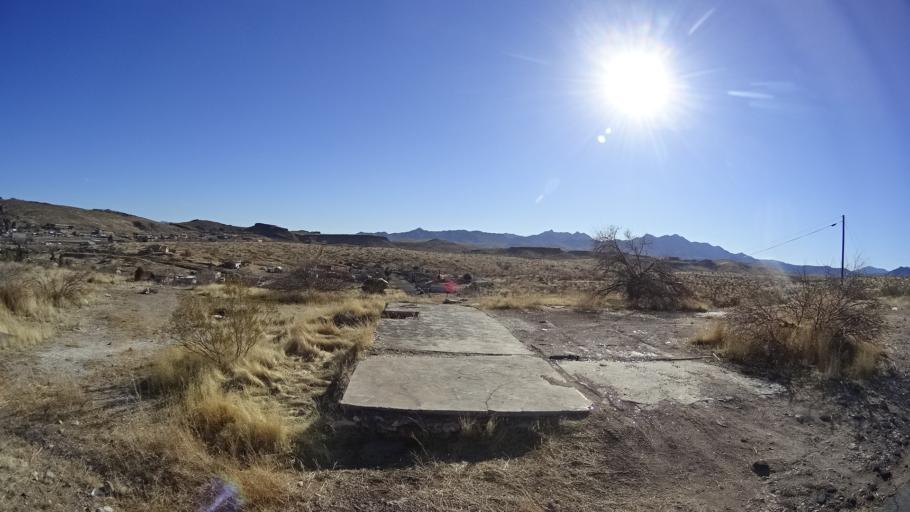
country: US
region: Arizona
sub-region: Mohave County
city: Kingman
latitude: 35.1826
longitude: -114.0527
